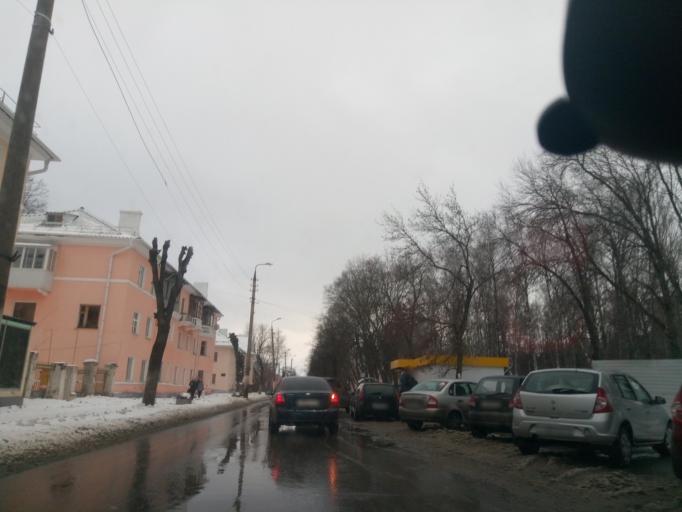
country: RU
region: Tula
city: Novomoskovsk
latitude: 54.0103
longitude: 38.2852
